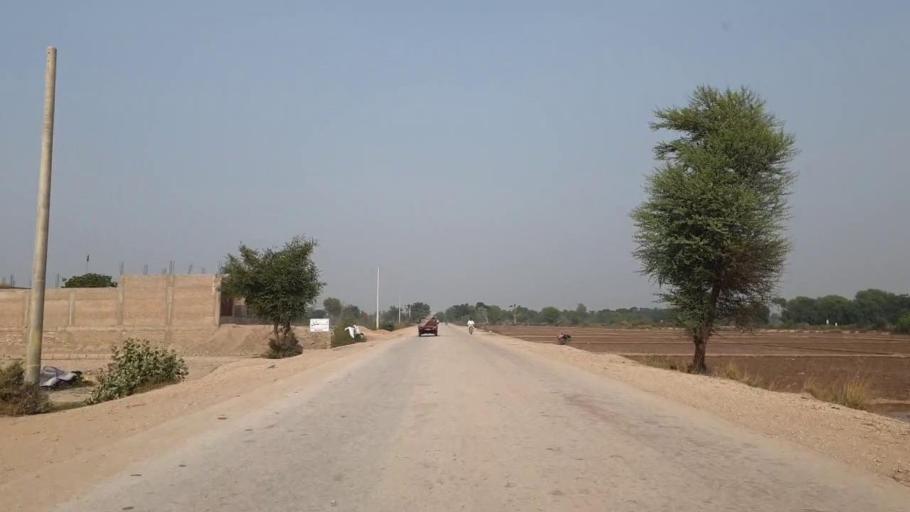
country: PK
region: Sindh
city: Bhan
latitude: 26.5698
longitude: 67.7259
